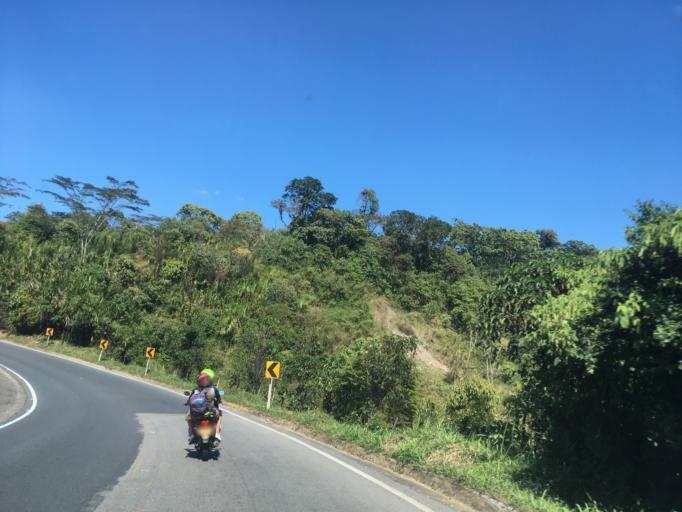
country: CO
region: Santander
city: Suaita
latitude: 6.0848
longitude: -73.3866
